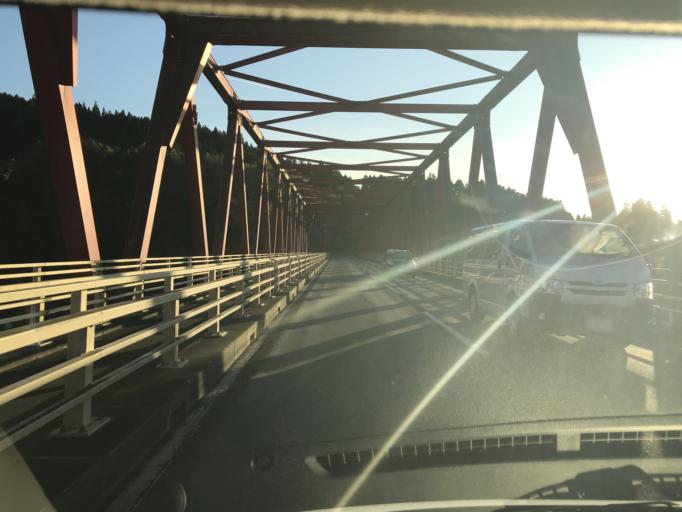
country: JP
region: Iwate
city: Ichinoseki
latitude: 38.9494
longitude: 141.1814
